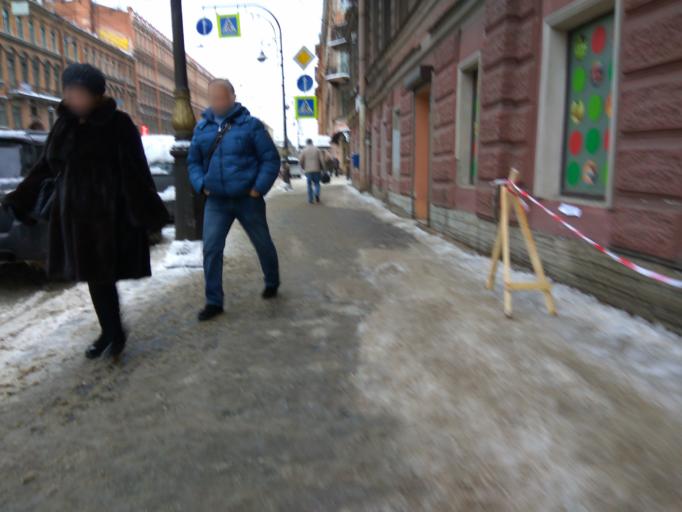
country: RU
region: St.-Petersburg
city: Centralniy
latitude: 59.9310
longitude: 30.3478
